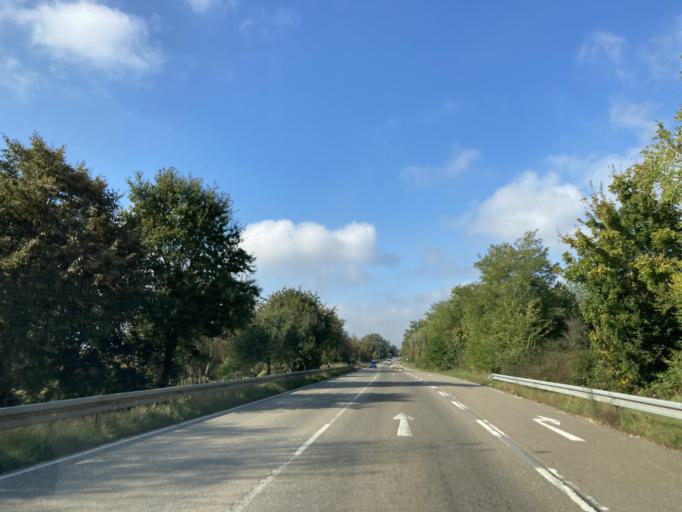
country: DE
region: Baden-Wuerttemberg
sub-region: Freiburg Region
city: Eschbach
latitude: 47.8871
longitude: 7.6206
